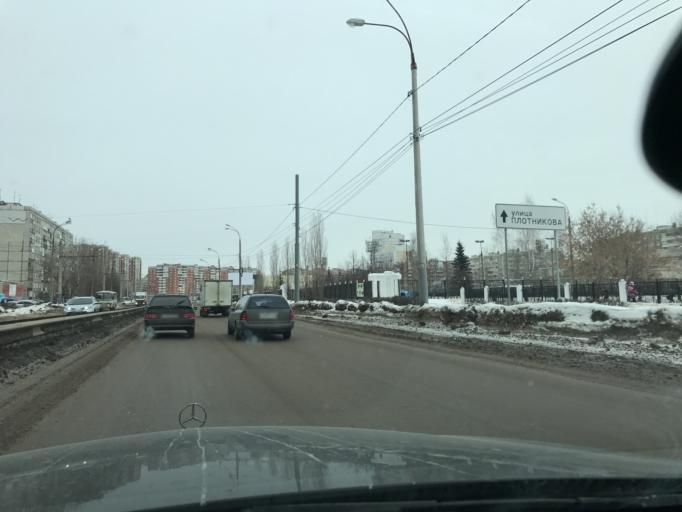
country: RU
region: Nizjnij Novgorod
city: Gorbatovka
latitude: 56.2542
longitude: 43.8528
